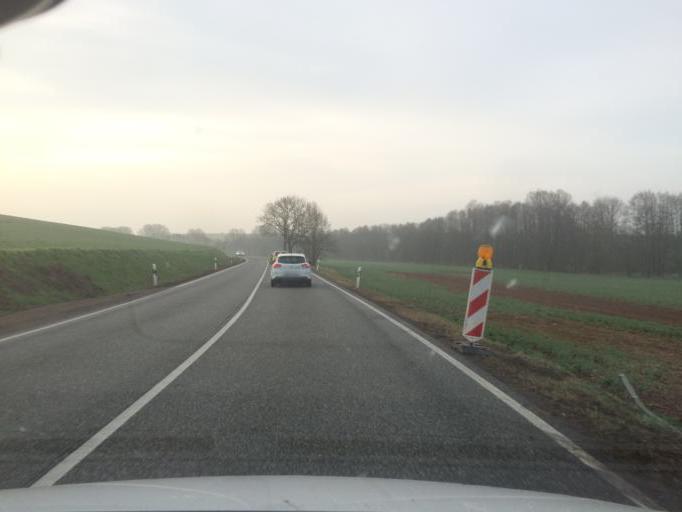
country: DE
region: Thuringia
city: Etzelsrode
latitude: 51.5242
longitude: 10.6397
